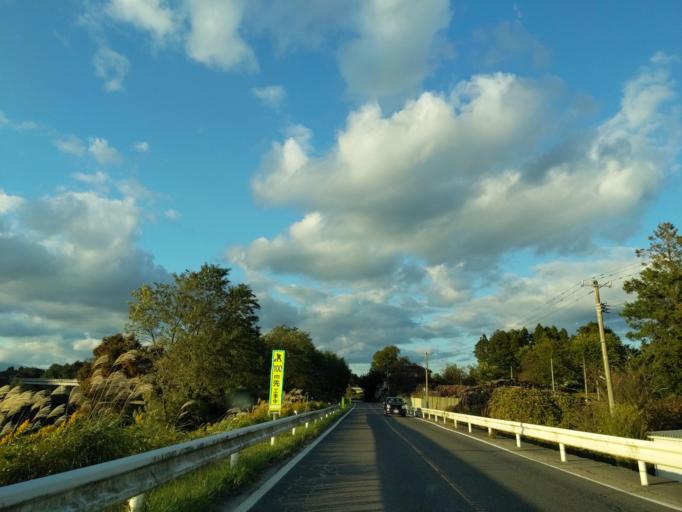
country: JP
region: Fukushima
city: Koriyama
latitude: 37.4393
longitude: 140.4234
